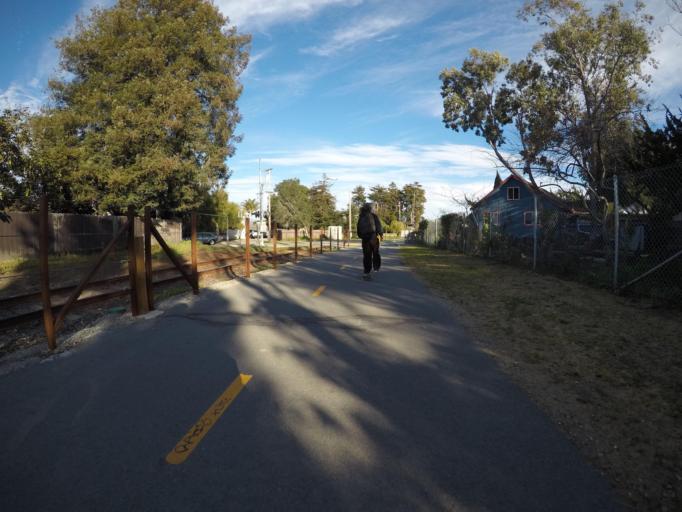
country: US
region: California
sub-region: Santa Cruz County
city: Santa Cruz
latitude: 36.9638
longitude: -122.0367
